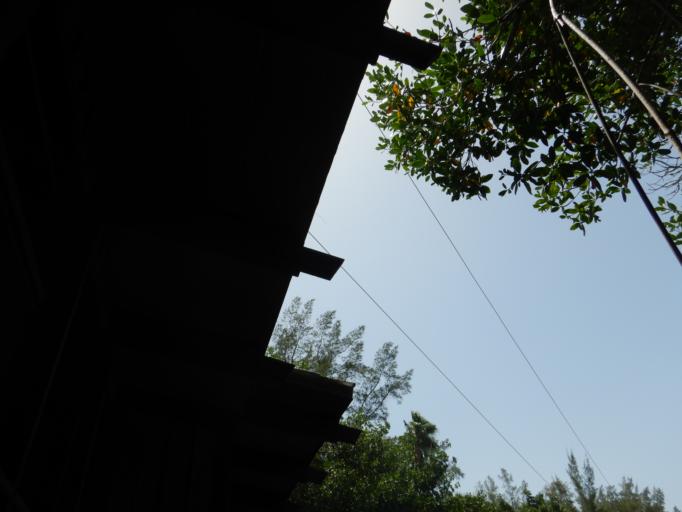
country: US
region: Florida
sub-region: Sarasota County
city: Vamo
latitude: 27.2279
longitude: -82.5208
